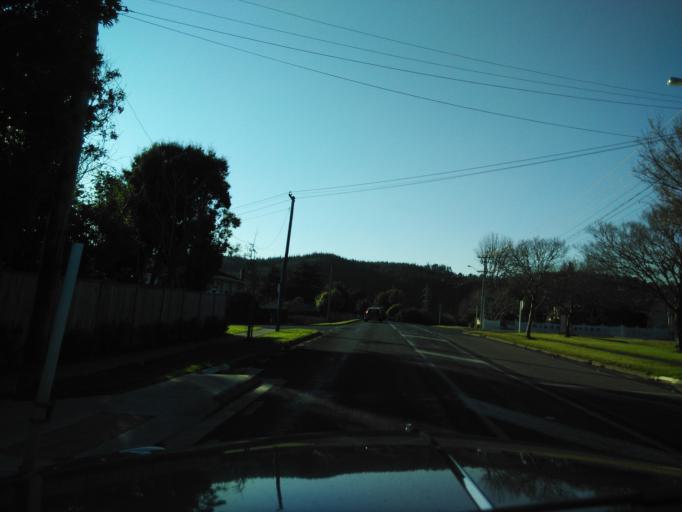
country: NZ
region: Auckland
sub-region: Auckland
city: Rosebank
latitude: -36.7567
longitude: 174.5917
